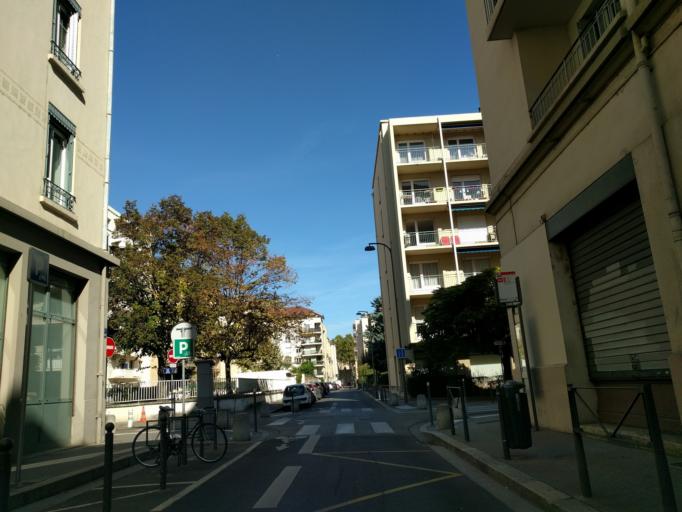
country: FR
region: Rhone-Alpes
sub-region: Departement du Rhone
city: Lyon
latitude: 45.7438
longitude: 4.8241
